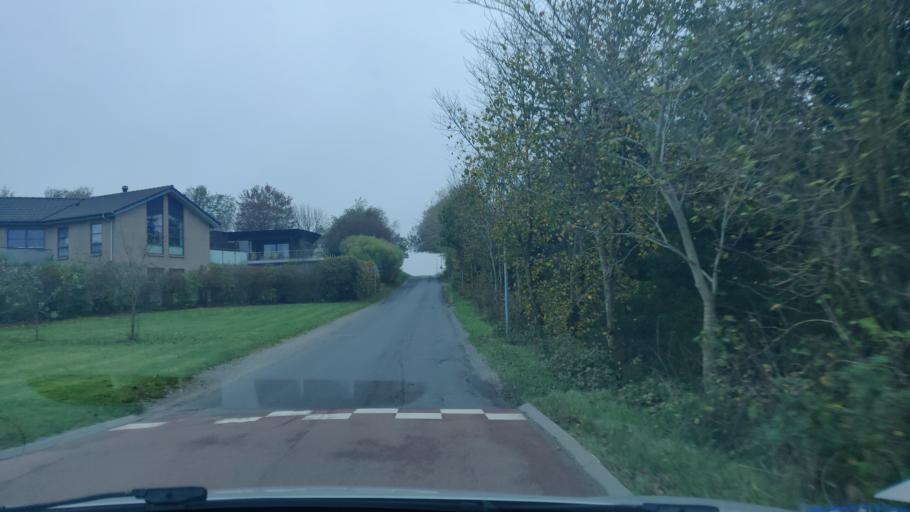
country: DK
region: South Denmark
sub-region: Kolding Kommune
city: Kolding
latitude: 55.5657
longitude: 9.4153
